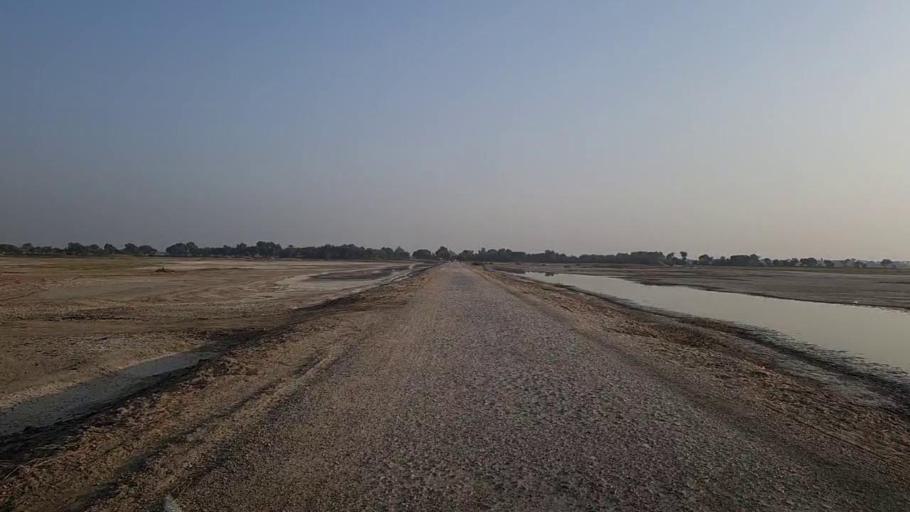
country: PK
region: Sindh
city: Kandhkot
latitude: 28.2465
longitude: 69.0905
